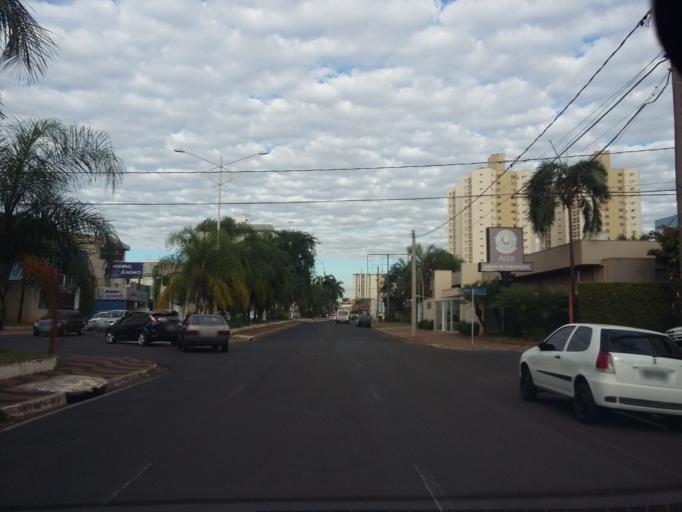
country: BR
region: Sao Paulo
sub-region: Sao Jose Do Rio Preto
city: Sao Jose do Rio Preto
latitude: -20.8142
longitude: -49.3910
